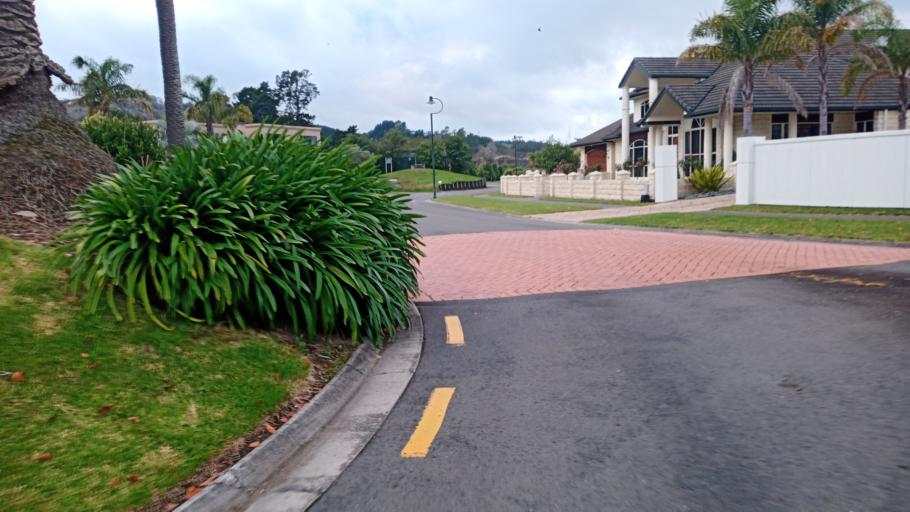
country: NZ
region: Gisborne
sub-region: Gisborne District
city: Gisborne
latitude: -38.6420
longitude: 178.0166
